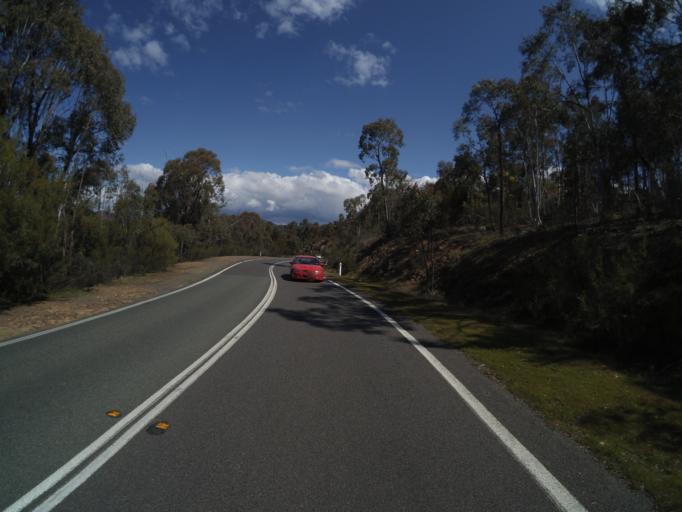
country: AU
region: Australian Capital Territory
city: Macquarie
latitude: -35.3125
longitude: 148.9481
